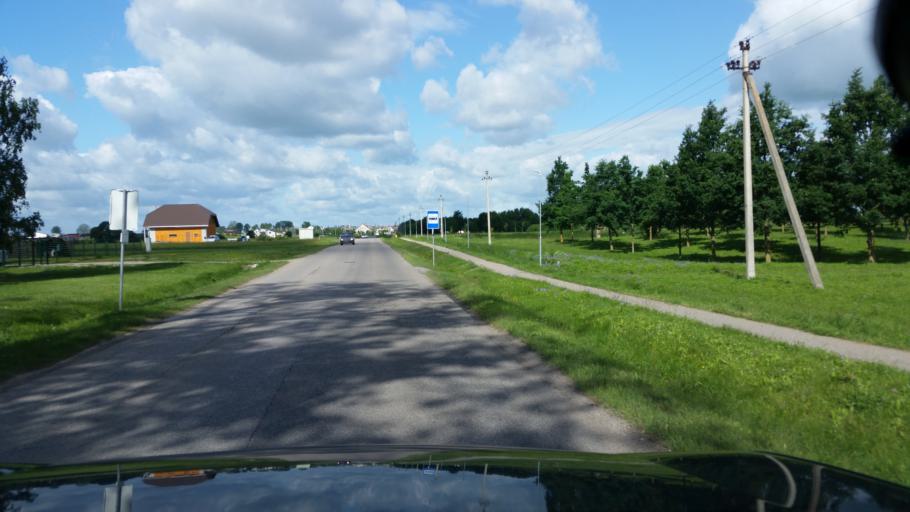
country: LT
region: Marijampoles apskritis
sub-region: Marijampole Municipality
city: Marijampole
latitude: 54.5514
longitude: 23.3235
